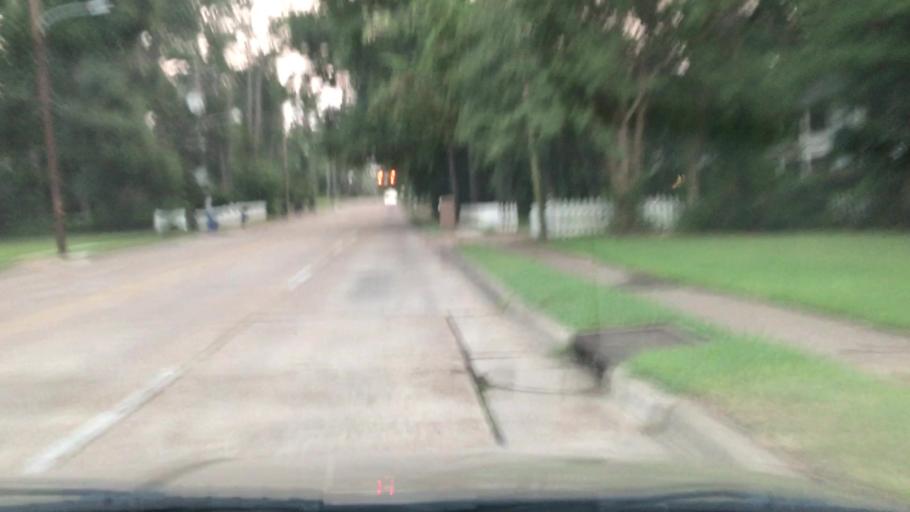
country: US
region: Louisiana
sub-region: Bossier Parish
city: Bossier City
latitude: 32.4546
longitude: -93.7436
